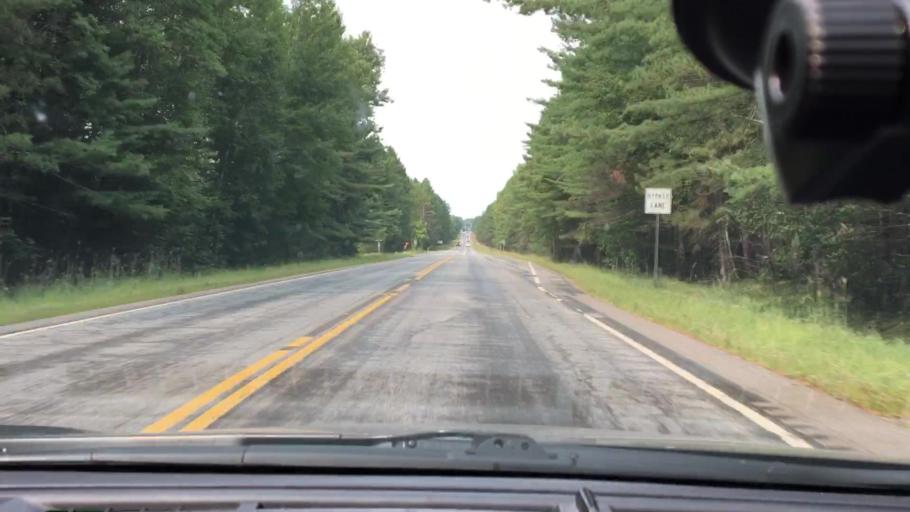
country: US
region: Minnesota
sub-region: Crow Wing County
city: Cross Lake
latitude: 46.7768
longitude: -93.9663
